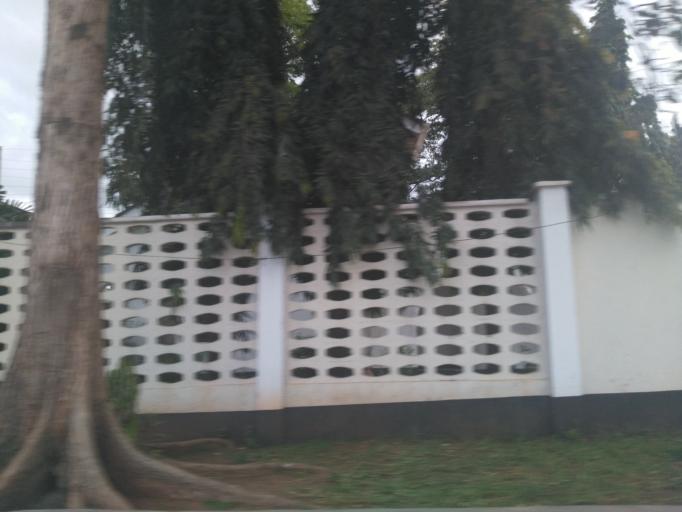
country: TZ
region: Dar es Salaam
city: Magomeni
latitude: -6.7782
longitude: 39.2674
